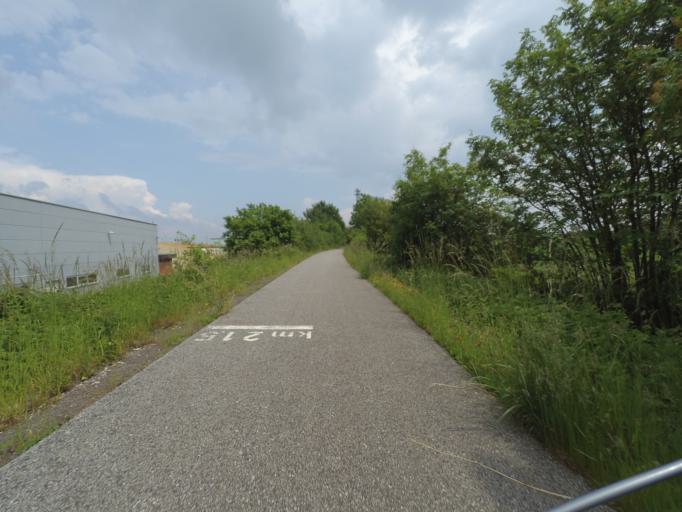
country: DE
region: Rheinland-Pfalz
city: Roth
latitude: 50.0734
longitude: 7.4539
